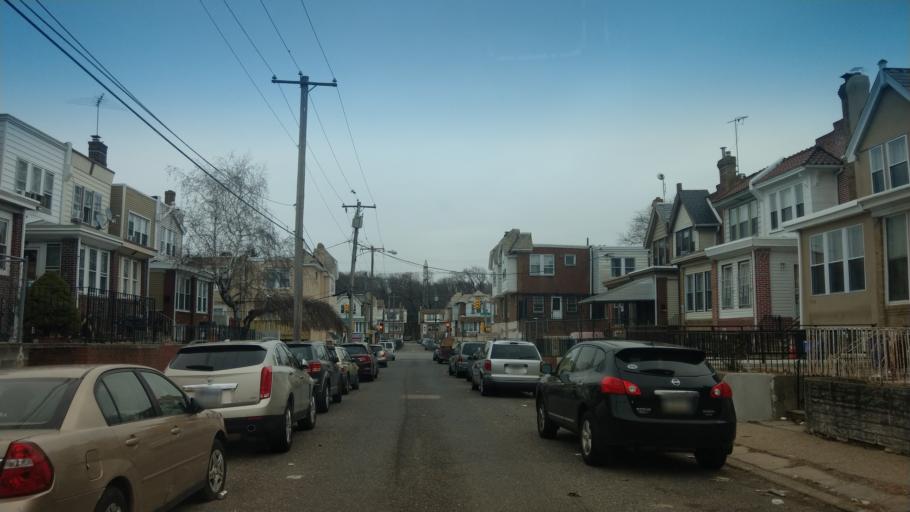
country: US
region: Pennsylvania
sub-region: Montgomery County
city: Rockledge
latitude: 40.0269
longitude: -75.1089
